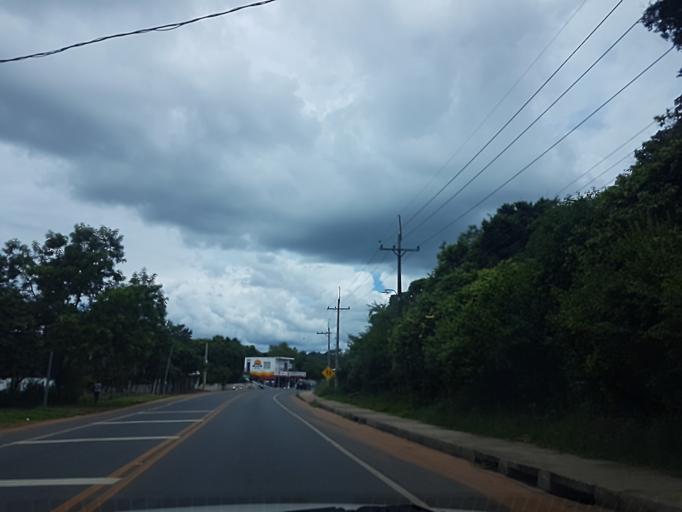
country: PY
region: Central
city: Limpio
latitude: -25.2360
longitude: -57.4429
